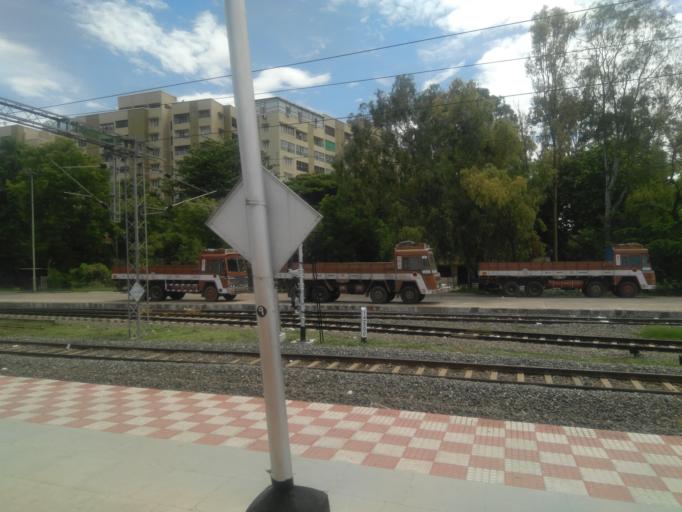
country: IN
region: Tamil Nadu
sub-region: Coimbatore
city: Coimbatore
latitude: 11.0225
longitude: 76.9539
